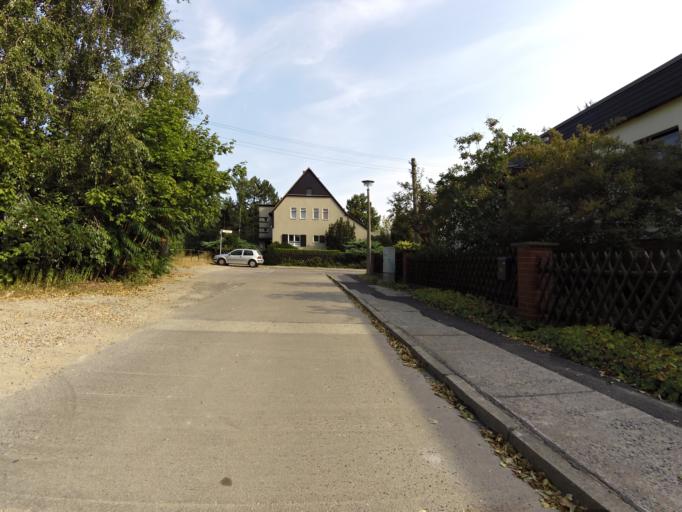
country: DE
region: Berlin
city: Bohnsdorf
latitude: 52.4101
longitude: 13.5606
